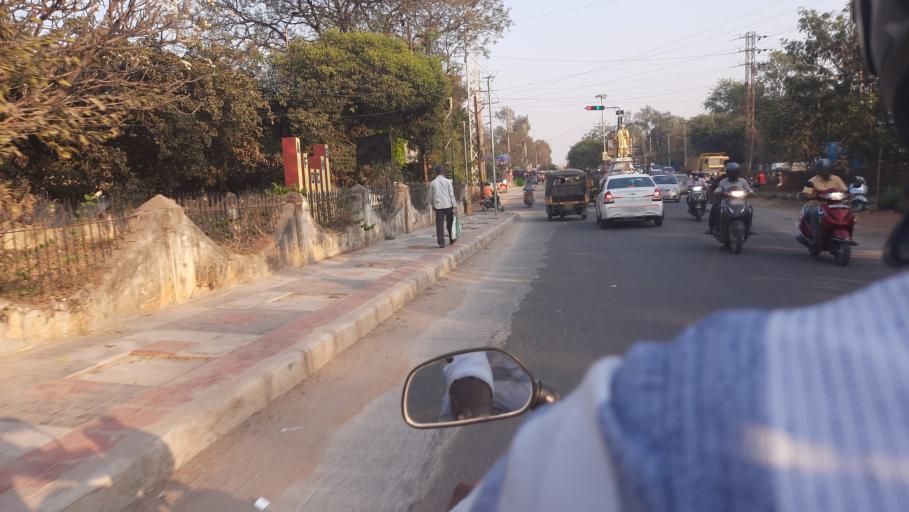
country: IN
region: Telangana
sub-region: Rangareddi
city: Secunderabad
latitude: 17.4845
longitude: 78.5485
